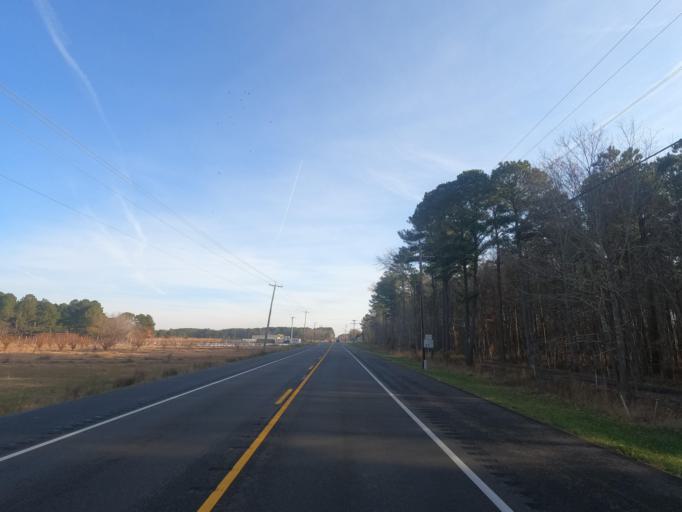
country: US
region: Maryland
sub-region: Somerset County
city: Crisfield
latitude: 38.0316
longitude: -75.7833
